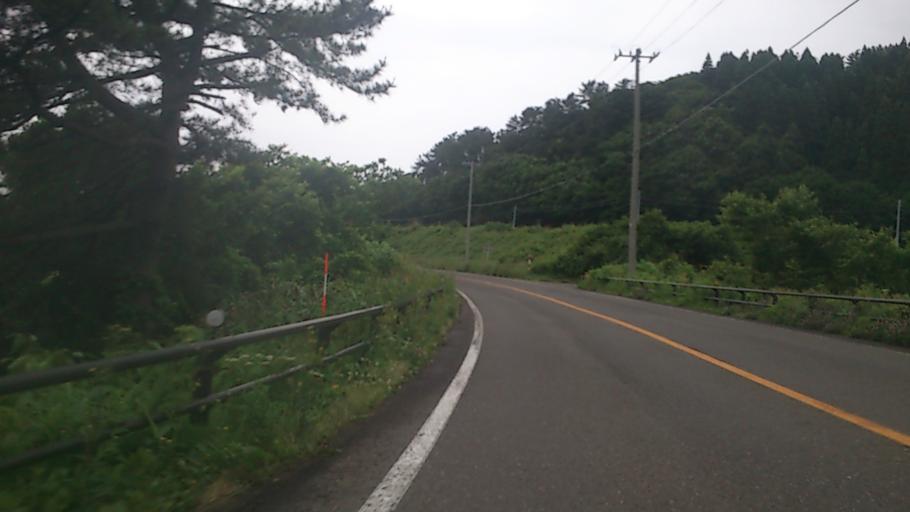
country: JP
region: Akita
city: Noshiromachi
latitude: 40.3778
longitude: 140.0127
